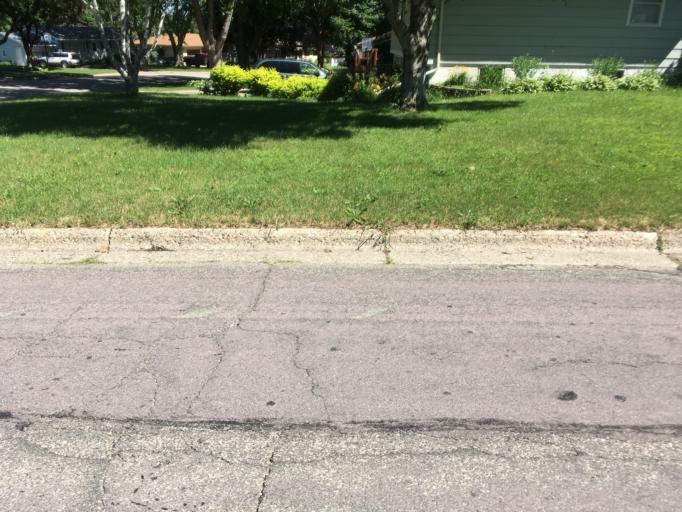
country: US
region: Minnesota
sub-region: Rice County
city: Faribault
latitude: 44.2784
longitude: -93.2912
